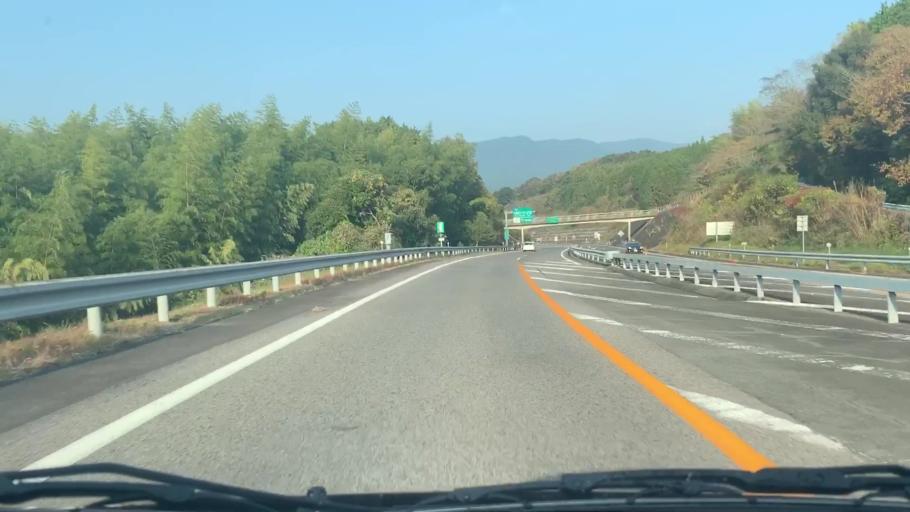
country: JP
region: Saga Prefecture
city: Imaricho-ko
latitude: 33.1668
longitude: 129.8569
